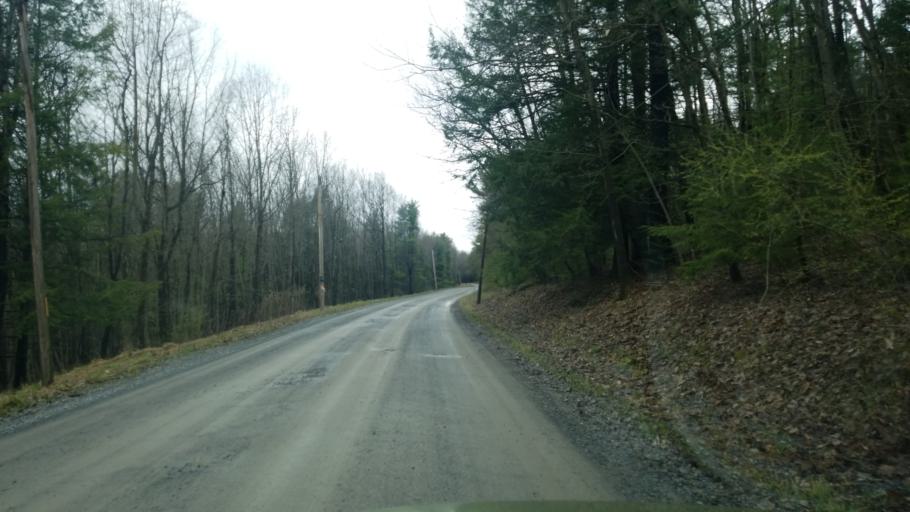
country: US
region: Pennsylvania
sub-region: Clearfield County
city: Shiloh
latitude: 41.1354
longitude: -78.3343
